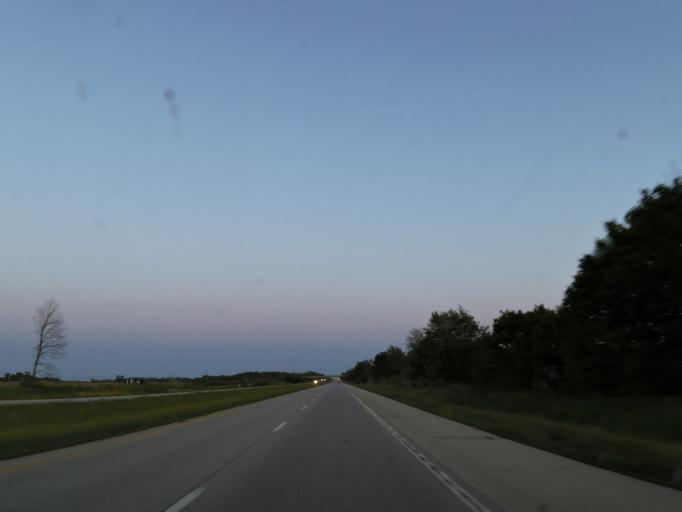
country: US
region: Indiana
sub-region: Boone County
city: Thorntown
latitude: 39.9702
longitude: -86.6578
